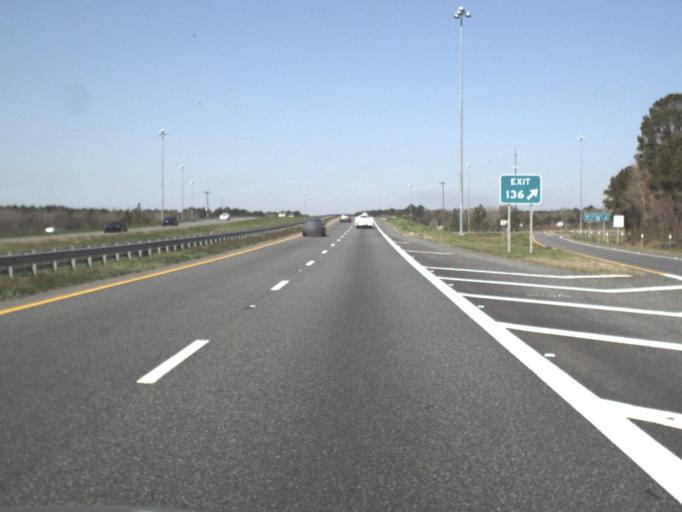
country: US
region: Florida
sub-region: Jackson County
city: Marianna
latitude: 30.7515
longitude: -85.2686
